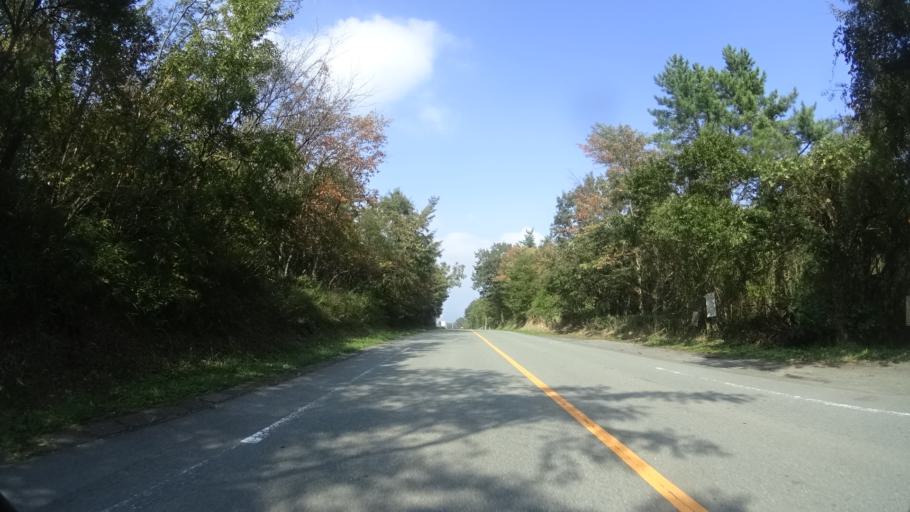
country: JP
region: Kumamoto
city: Aso
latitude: 33.0310
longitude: 131.0639
